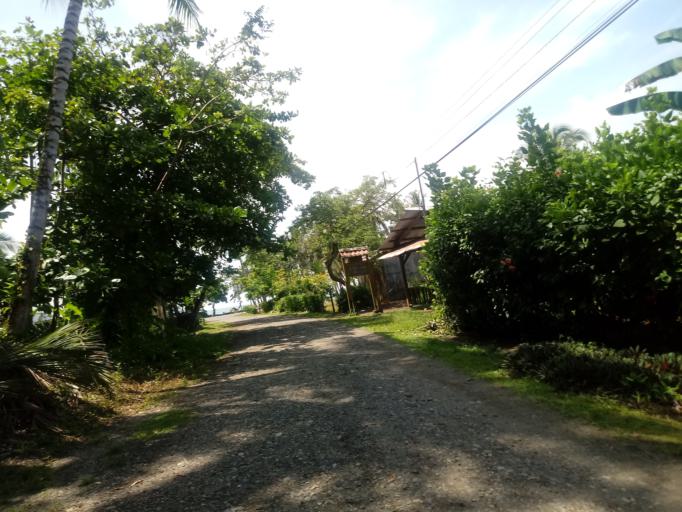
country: CR
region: Limon
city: Sixaola
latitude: 9.6317
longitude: -82.6584
